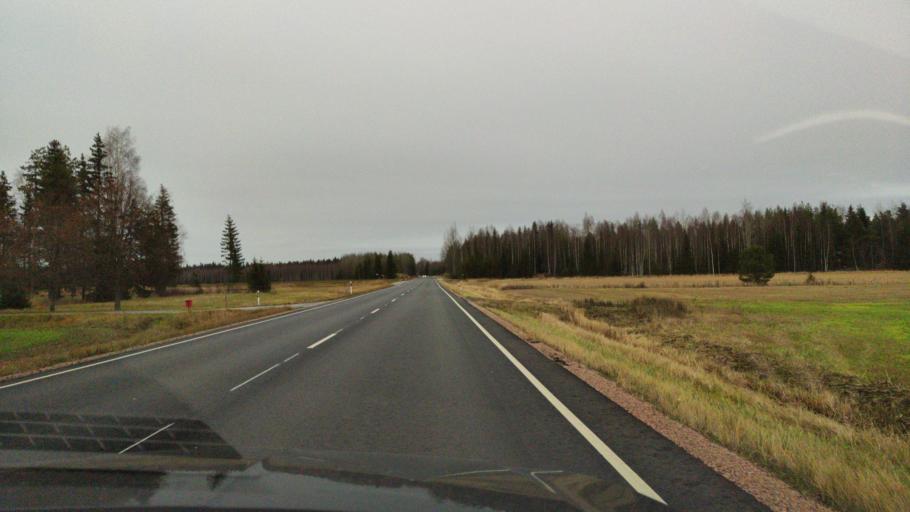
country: FI
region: Varsinais-Suomi
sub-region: Loimaa
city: Aura
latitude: 60.7105
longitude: 22.4433
